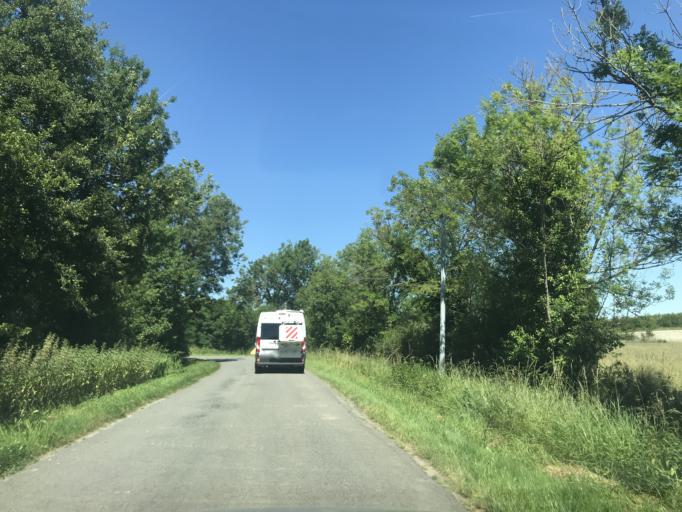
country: FR
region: Poitou-Charentes
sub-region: Departement de la Charente-Maritime
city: Mortagne-sur-Gironde
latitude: 45.4246
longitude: -0.7390
